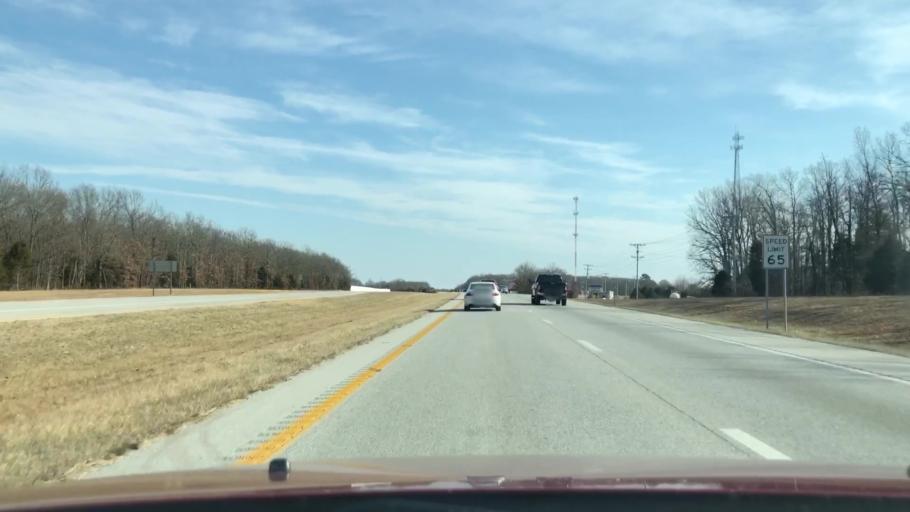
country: US
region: Missouri
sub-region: Webster County
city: Rogersville
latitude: 37.1169
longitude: -93.0218
